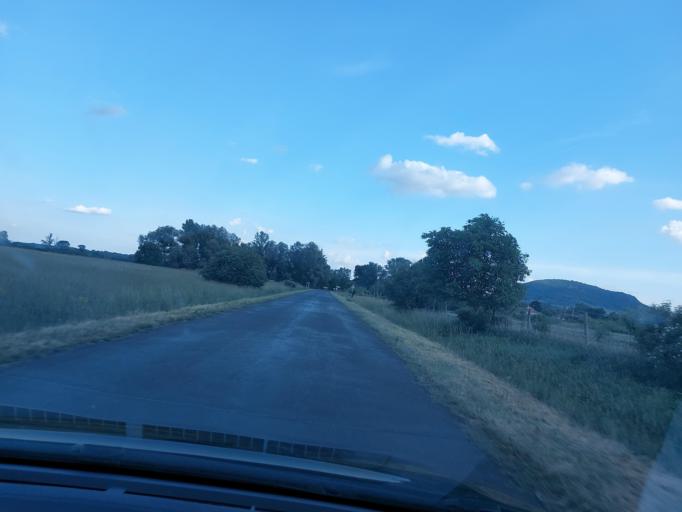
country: HU
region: Veszprem
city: Devecser
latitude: 47.1810
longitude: 17.3625
